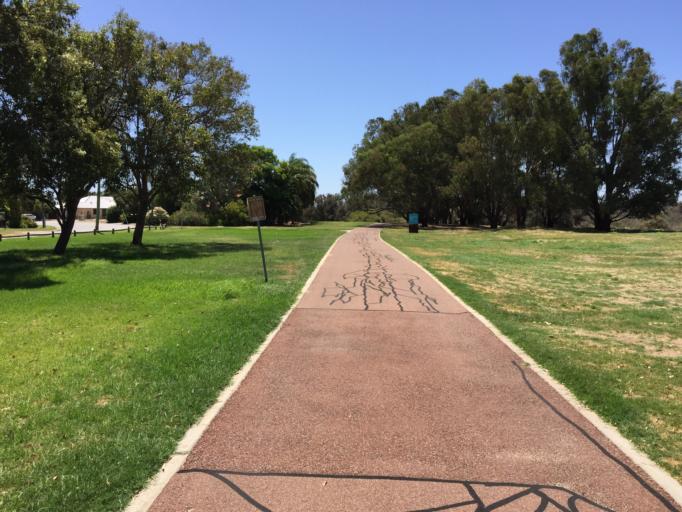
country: AU
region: Western Australia
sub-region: Canning
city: Wilson
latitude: -32.0333
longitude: 115.9046
